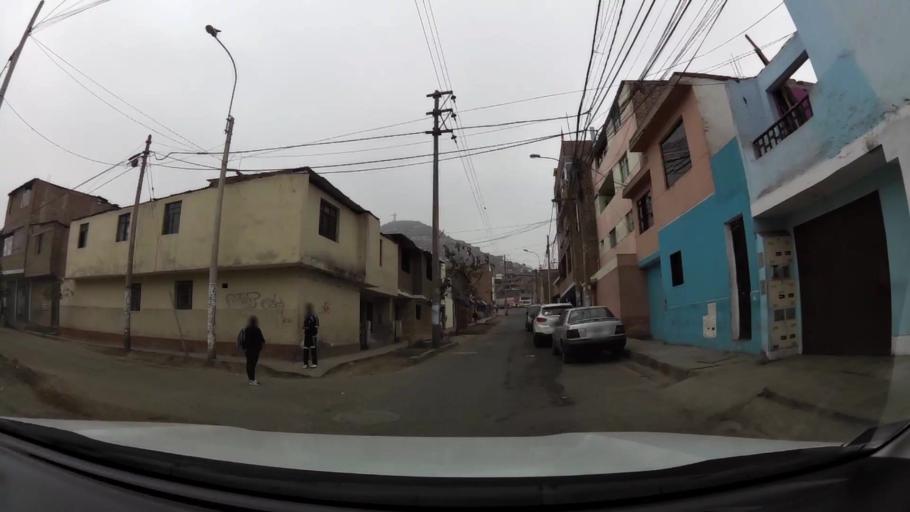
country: PE
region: Lima
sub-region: Lima
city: Surco
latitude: -12.1567
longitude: -76.9616
